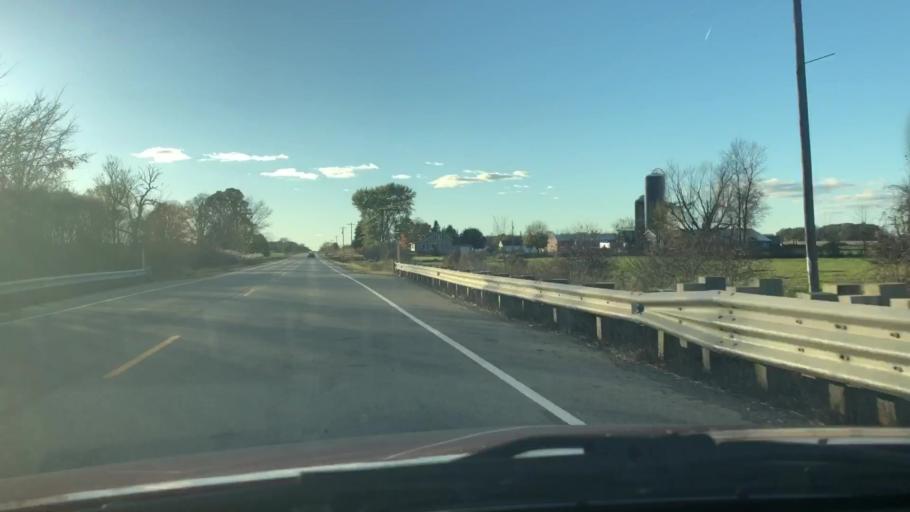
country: US
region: Wisconsin
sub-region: Brown County
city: Oneida
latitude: 44.4443
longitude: -88.1616
